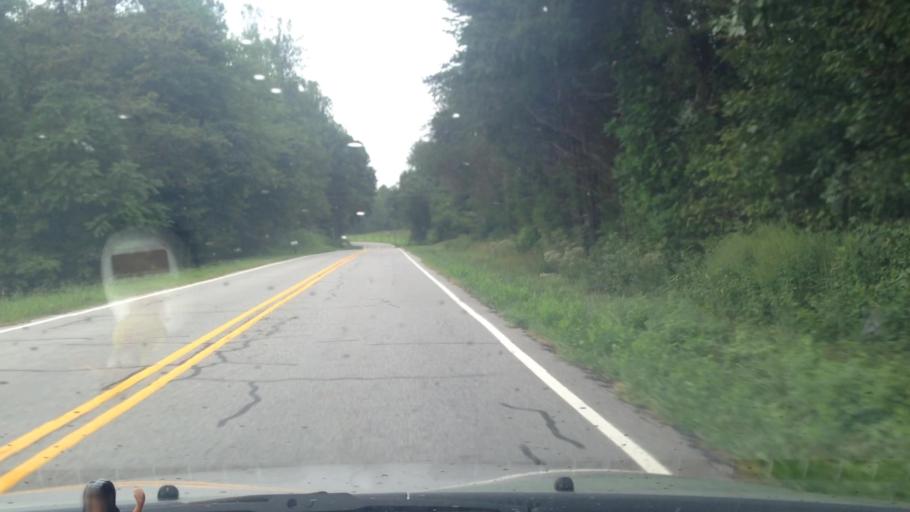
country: US
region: North Carolina
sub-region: Stokes County
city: Danbury
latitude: 36.4303
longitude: -80.1036
